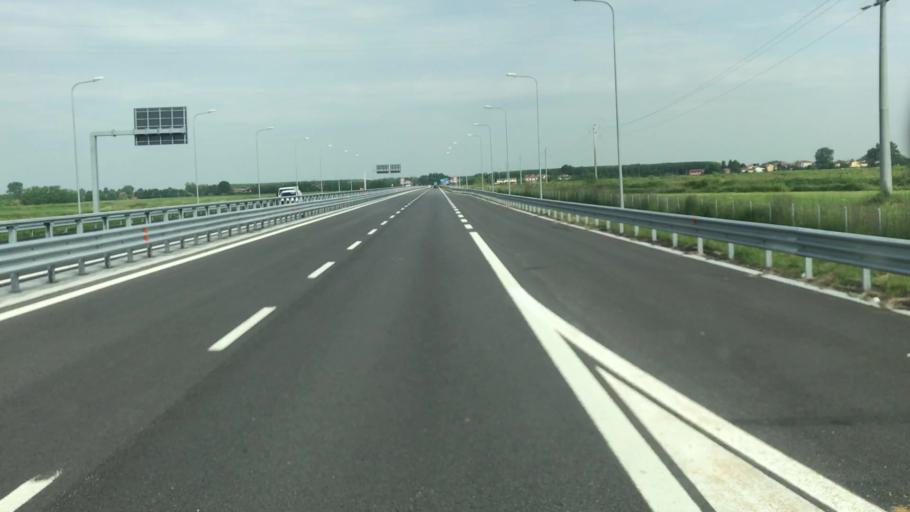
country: IT
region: Lombardy
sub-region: Provincia di Pavia
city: Torre d'Isola
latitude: 45.2217
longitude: 9.0821
